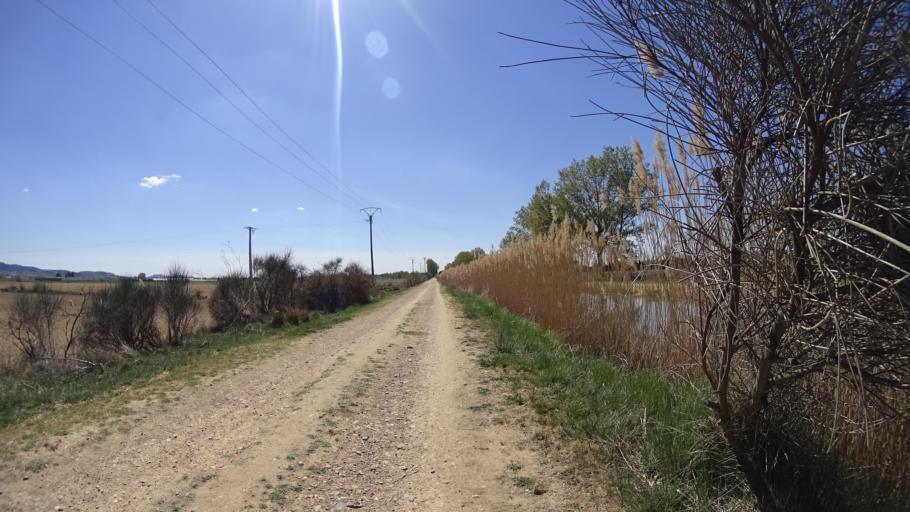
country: ES
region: Castille and Leon
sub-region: Provincia de Valladolid
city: Cabezon
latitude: 41.7399
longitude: -4.6641
